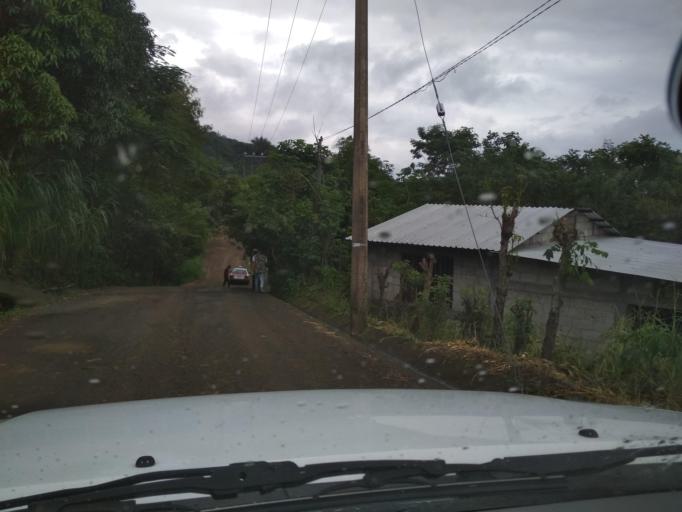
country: MX
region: Veracruz
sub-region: San Andres Tuxtla
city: San Isidro Xoteapan (San Isidro Texcaltitan)
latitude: 18.4645
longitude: -95.2368
